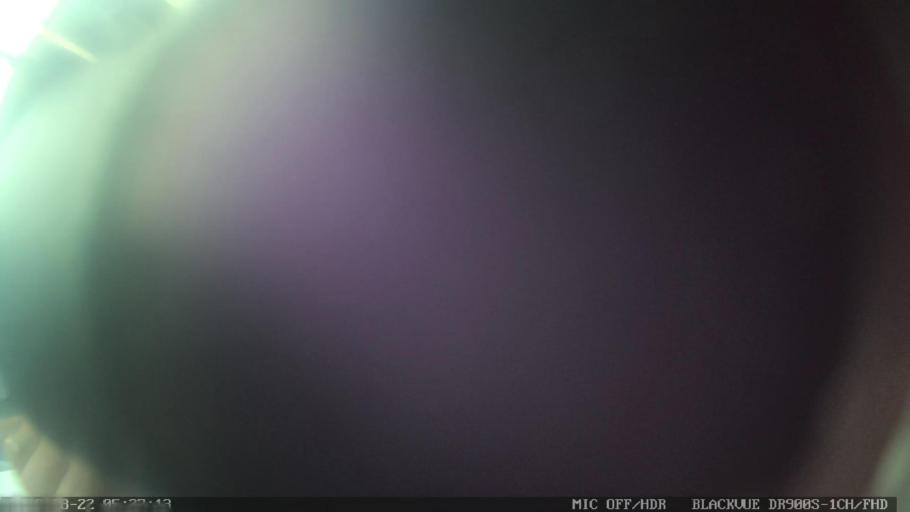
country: PT
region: Castelo Branco
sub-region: Idanha-A-Nova
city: Idanha-a-Nova
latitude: 39.9225
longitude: -7.2368
